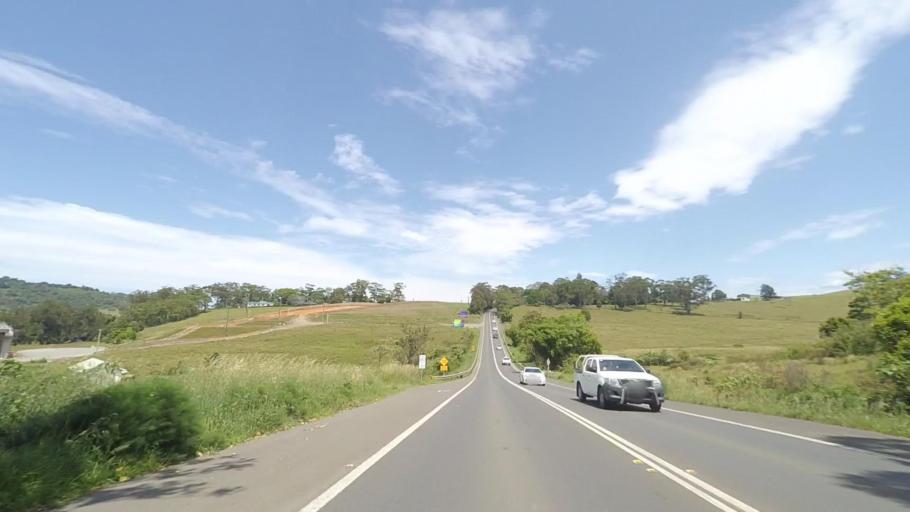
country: AU
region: New South Wales
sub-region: Shoalhaven Shire
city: Berry
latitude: -34.7539
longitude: 150.7496
